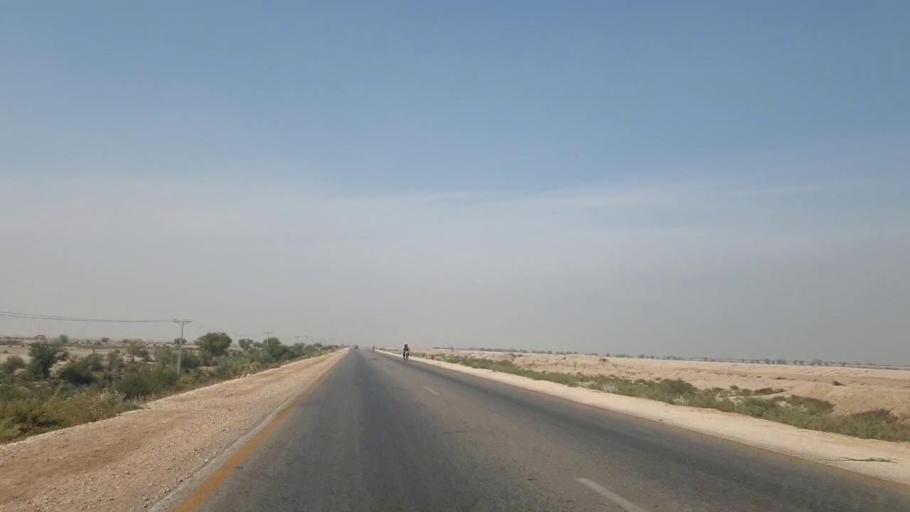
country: PK
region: Sindh
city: Sann
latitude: 25.9082
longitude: 68.2269
